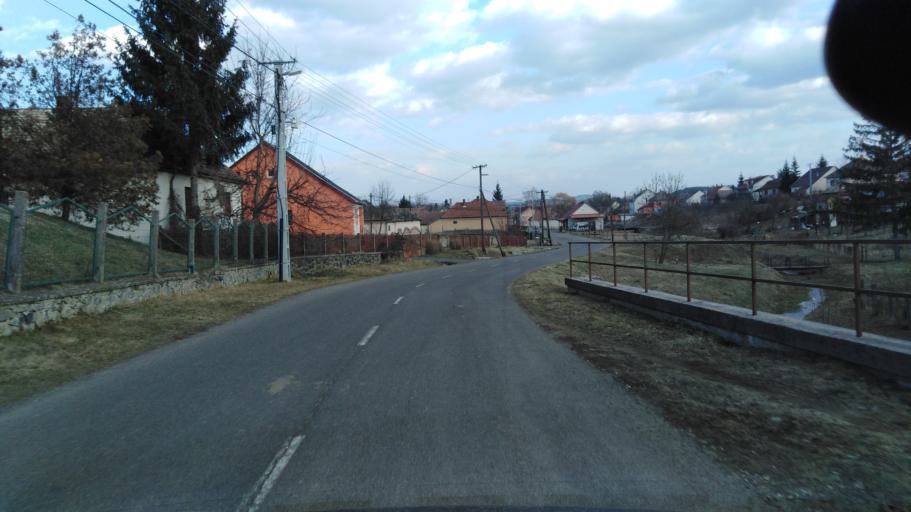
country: HU
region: Nograd
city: Matranovak
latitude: 48.1480
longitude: 19.9622
